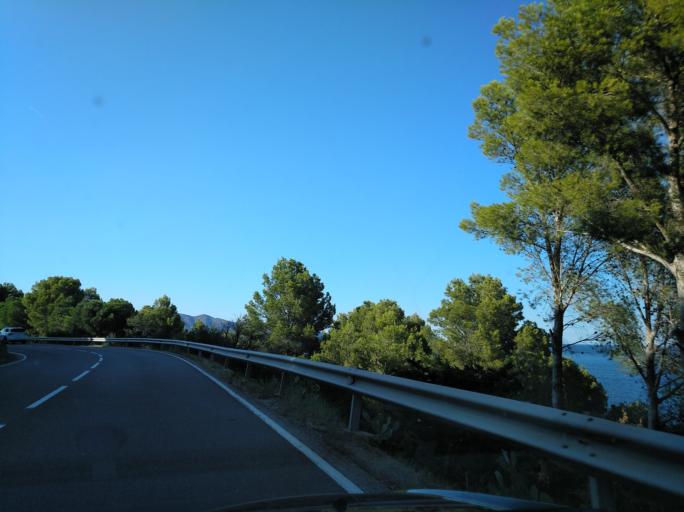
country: ES
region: Catalonia
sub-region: Provincia de Girona
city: Llanca
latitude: 42.3534
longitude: 3.1747
